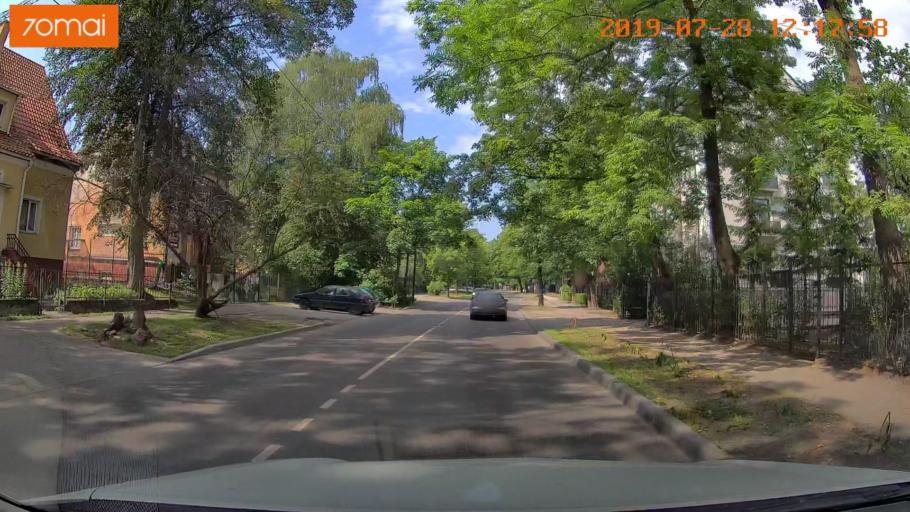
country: RU
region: Kaliningrad
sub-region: Gorod Kaliningrad
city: Kaliningrad
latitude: 54.7151
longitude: 20.4704
